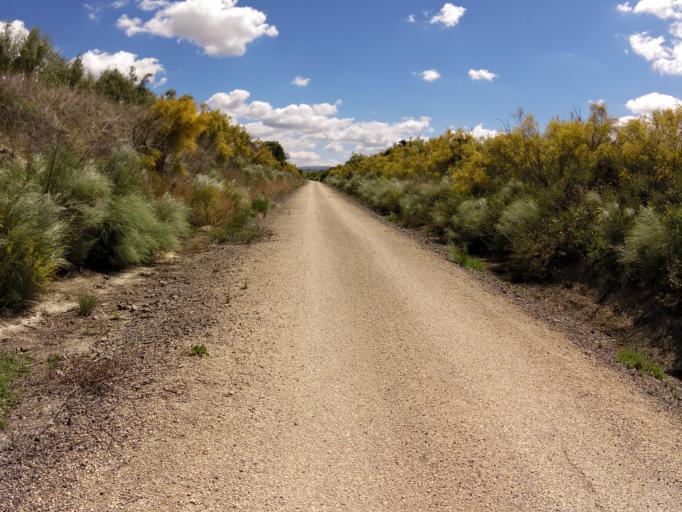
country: ES
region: Andalusia
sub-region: Provincia de Jaen
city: Alcaudete
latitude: 37.6462
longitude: -4.0745
